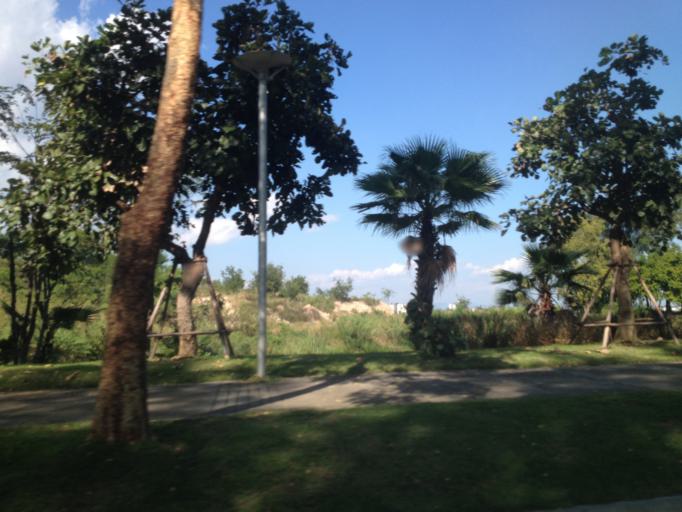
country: TH
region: Chiang Mai
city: Chiang Mai
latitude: 18.7498
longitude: 98.9480
